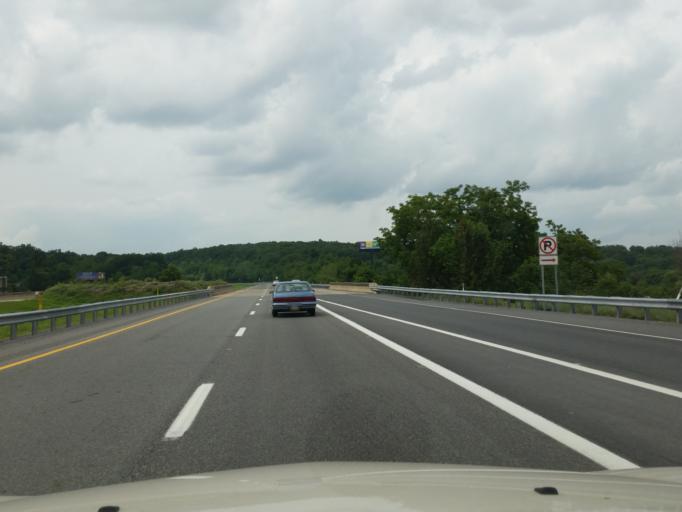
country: US
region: Pennsylvania
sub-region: Juniata County
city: Mifflintown
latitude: 40.5856
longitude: -77.3738
